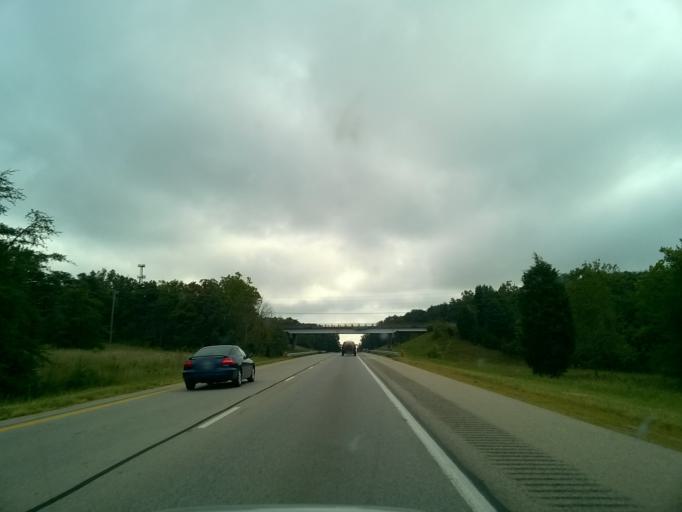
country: US
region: Indiana
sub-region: Floyd County
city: Georgetown
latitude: 38.2775
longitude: -85.9537
